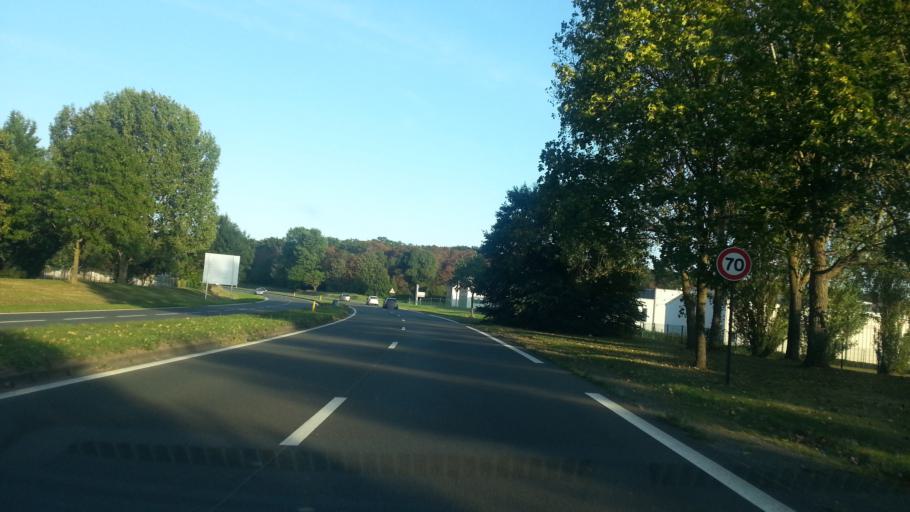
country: FR
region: Picardie
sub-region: Departement de l'Oise
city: Jaux
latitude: 49.3923
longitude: 2.7944
